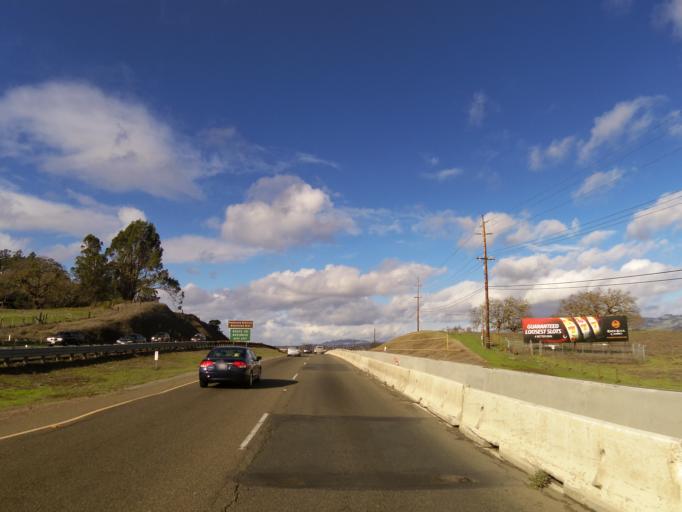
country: US
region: California
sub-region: Sonoma County
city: Petaluma
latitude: 38.2134
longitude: -122.6018
